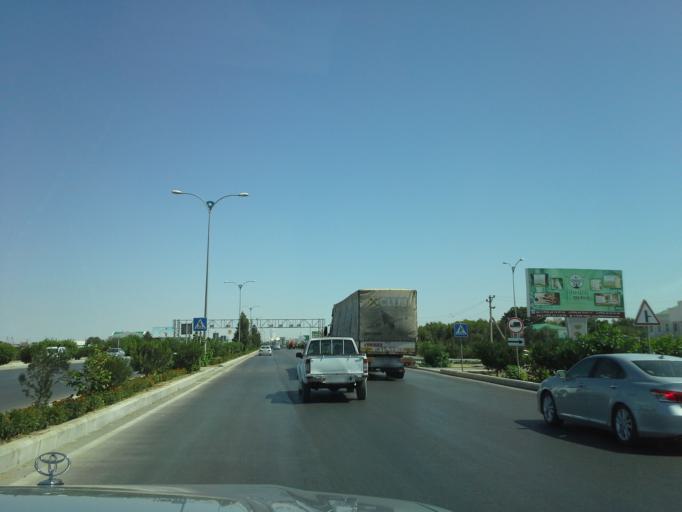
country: TM
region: Ahal
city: Annau
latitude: 37.9096
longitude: 58.5035
